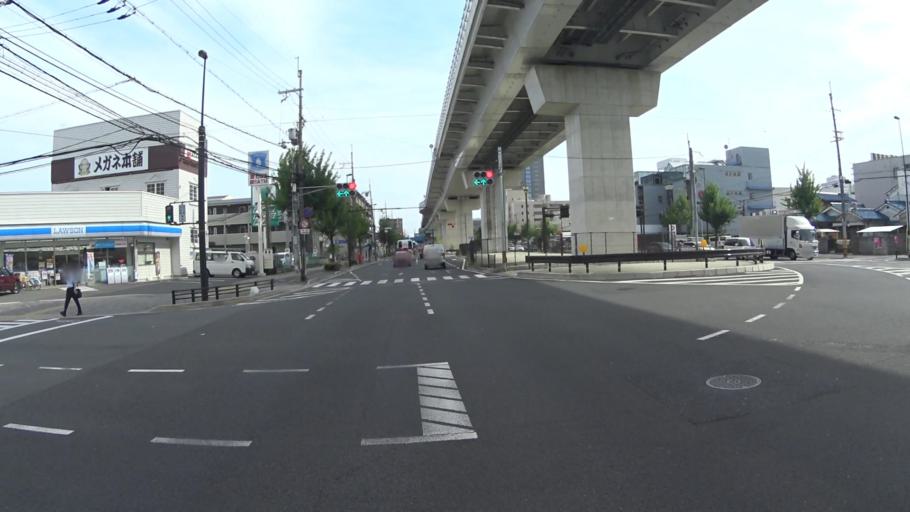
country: JP
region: Kyoto
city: Muko
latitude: 34.9517
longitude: 135.7521
